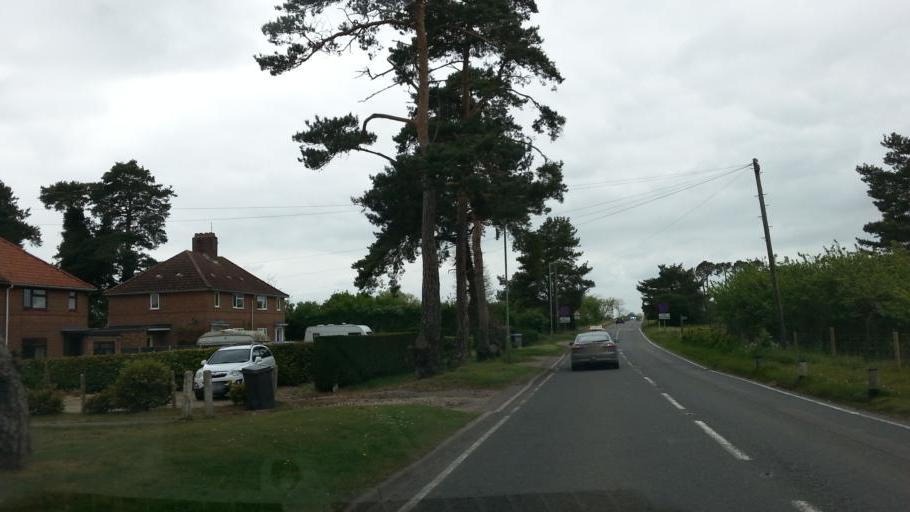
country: GB
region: England
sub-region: Suffolk
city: Lakenheath
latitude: 52.3299
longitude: 0.5917
